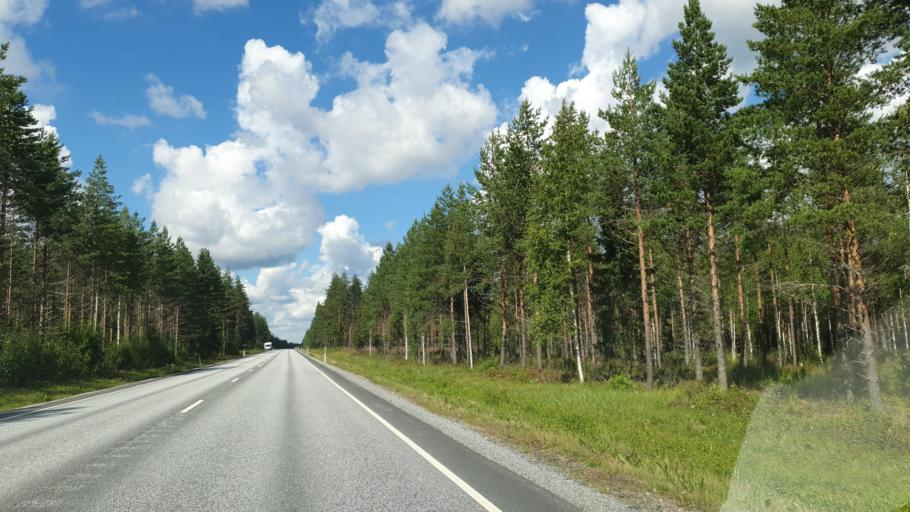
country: FI
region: Northern Savo
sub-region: Ylae-Savo
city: Sonkajaervi
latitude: 63.8927
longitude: 27.4185
